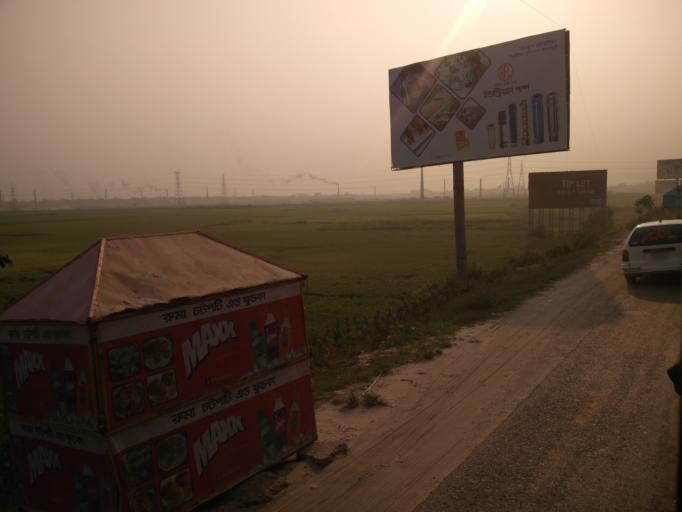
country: BD
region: Dhaka
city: Tungi
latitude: 23.8935
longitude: 90.3542
